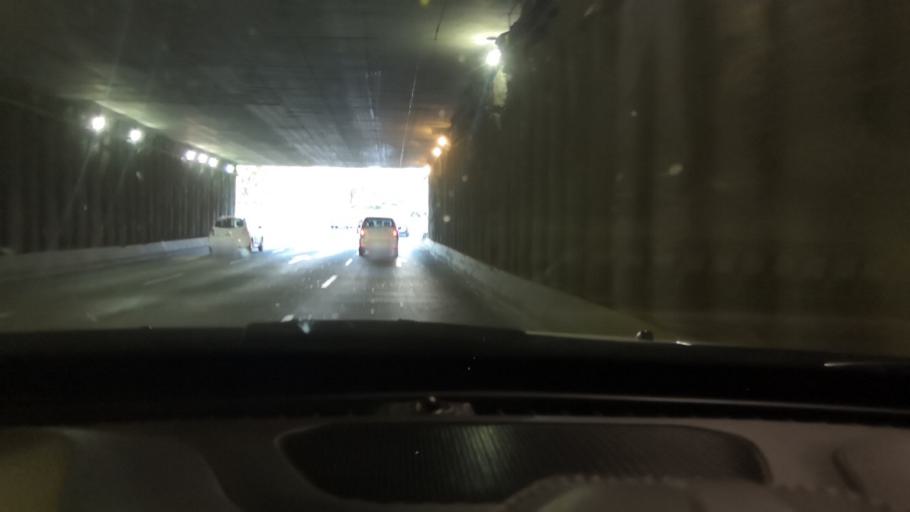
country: MX
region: Jalisco
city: Guadalajara
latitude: 20.6766
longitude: -103.4154
